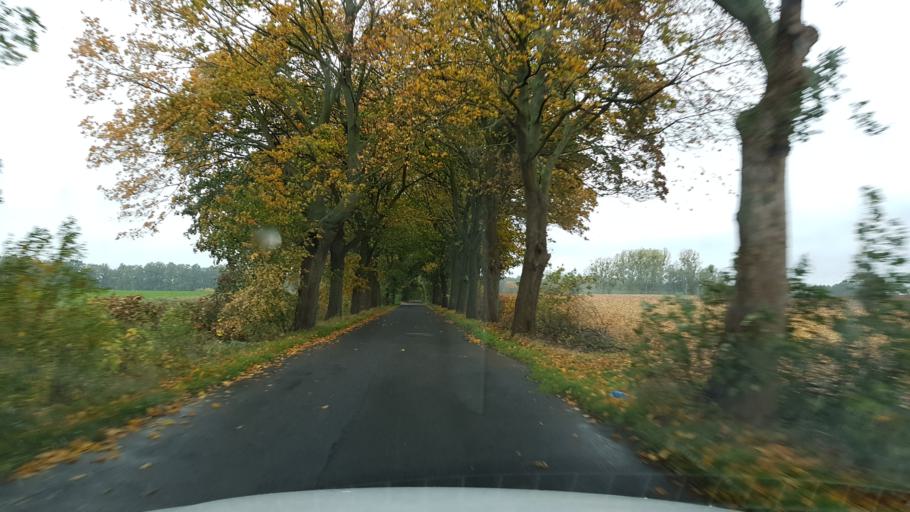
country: PL
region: West Pomeranian Voivodeship
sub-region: Powiat mysliborski
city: Mysliborz
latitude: 52.9796
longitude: 14.8717
